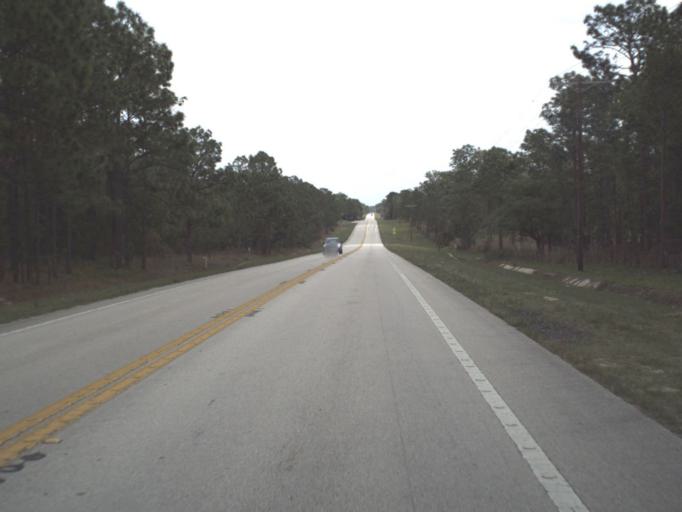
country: US
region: Florida
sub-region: Lake County
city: Mount Plymouth
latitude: 28.8554
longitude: -81.5212
